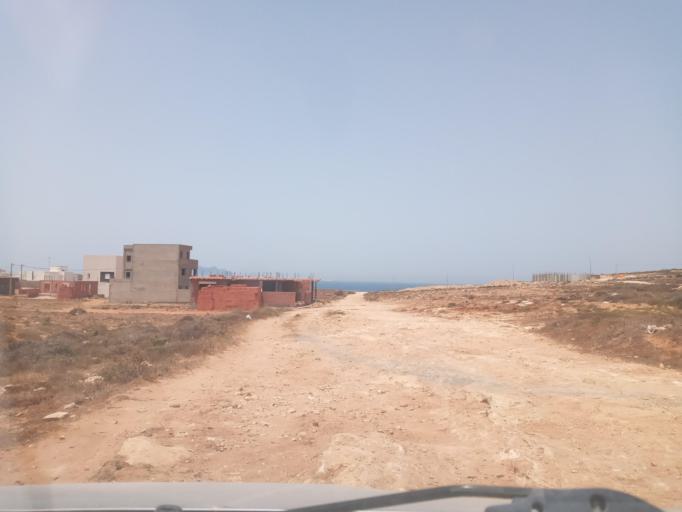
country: TN
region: Nabul
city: El Haouaria
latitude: 37.0538
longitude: 10.9985
